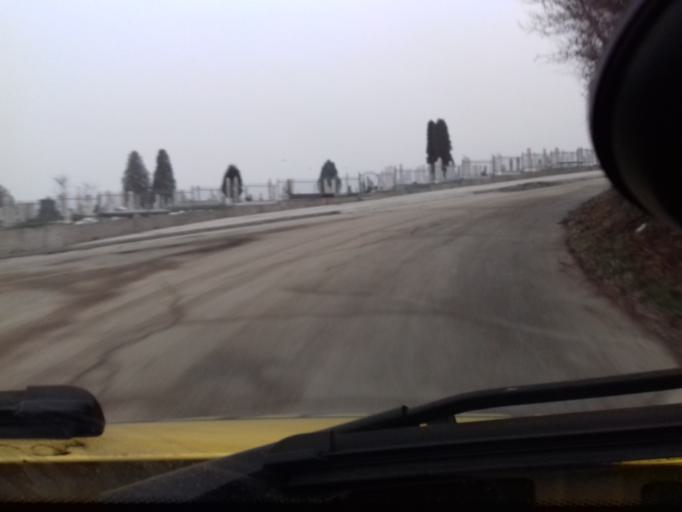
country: BA
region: Federation of Bosnia and Herzegovina
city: Zenica
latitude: 44.2123
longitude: 17.9267
